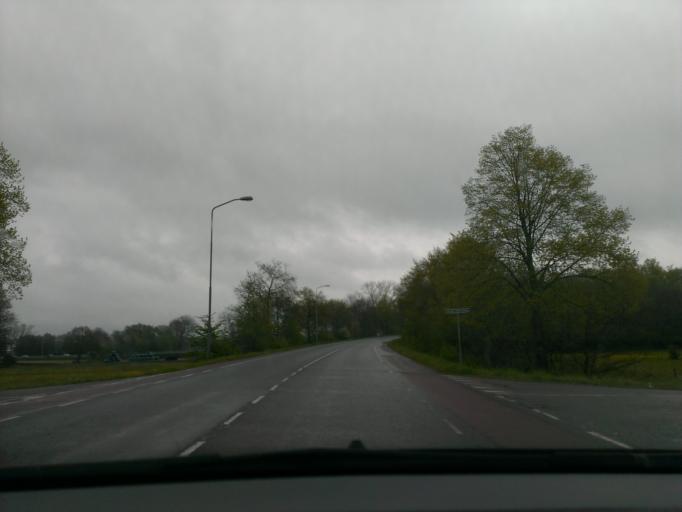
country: NL
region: Gelderland
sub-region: Gemeente Epe
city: Epe
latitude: 52.3469
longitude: 6.0118
